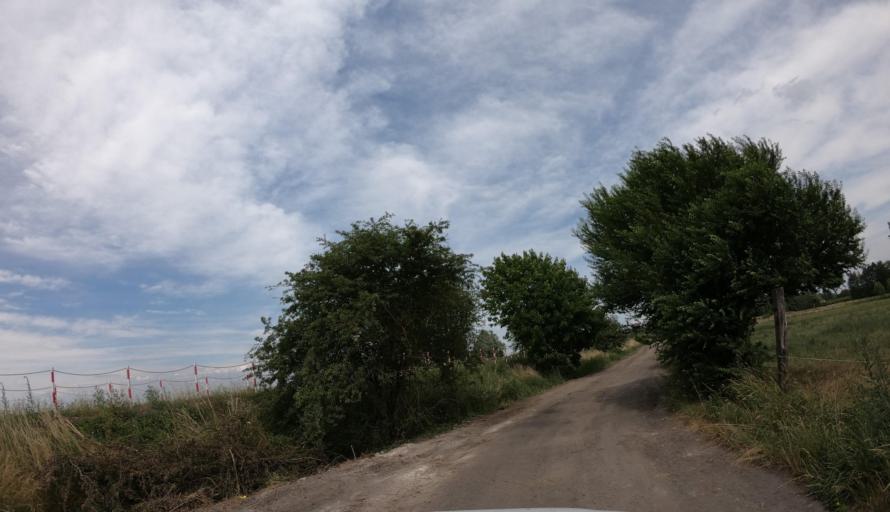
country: PL
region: West Pomeranian Voivodeship
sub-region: Powiat pyrzycki
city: Pyrzyce
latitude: 53.1404
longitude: 14.8695
